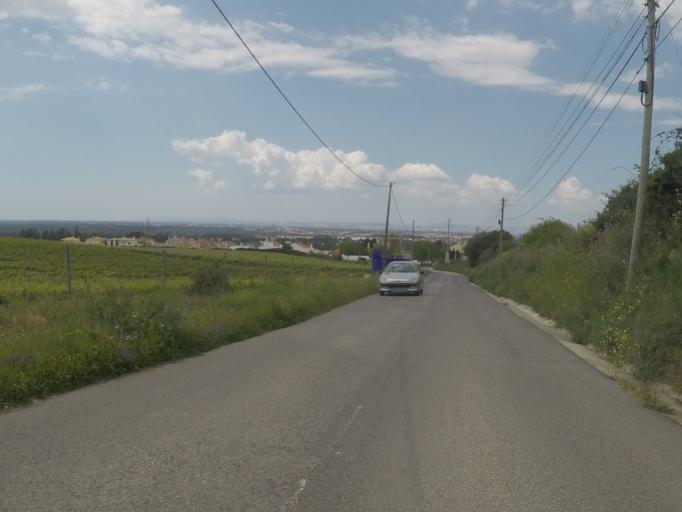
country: PT
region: Setubal
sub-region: Palmela
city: Quinta do Anjo
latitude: 38.5138
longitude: -9.0071
